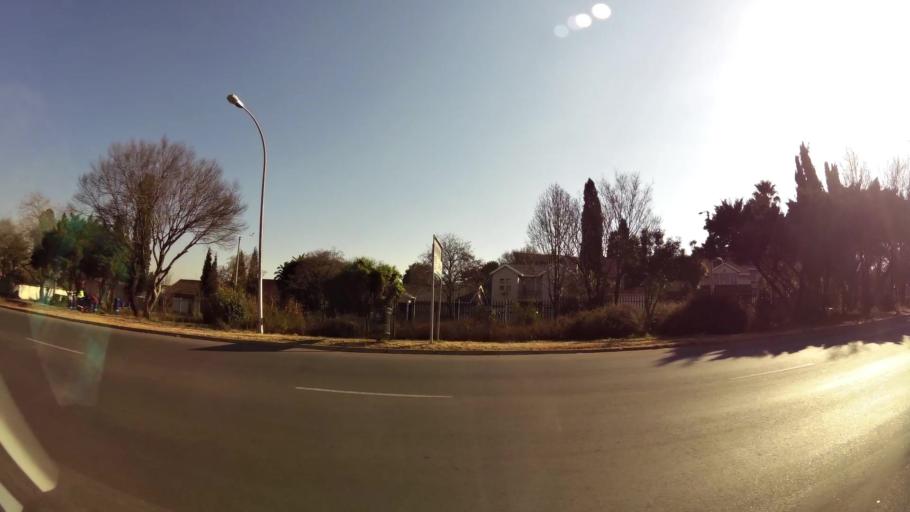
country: ZA
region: Gauteng
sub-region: City of Johannesburg Metropolitan Municipality
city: Modderfontein
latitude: -26.1617
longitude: 28.1517
